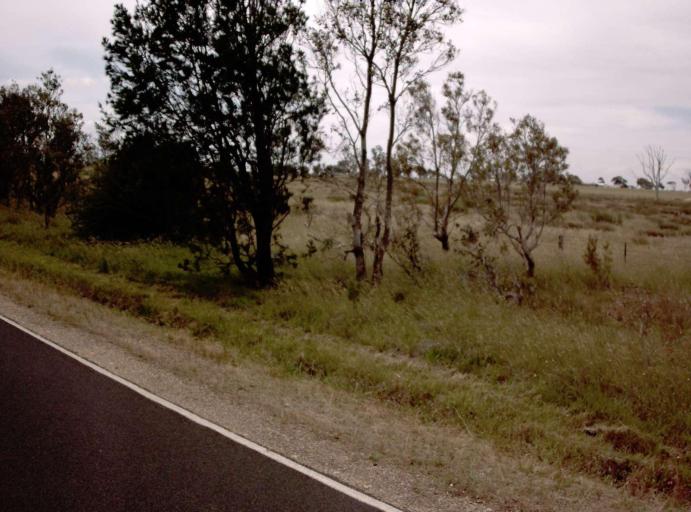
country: AU
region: Victoria
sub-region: Wellington
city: Sale
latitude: -37.9883
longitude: 147.1898
